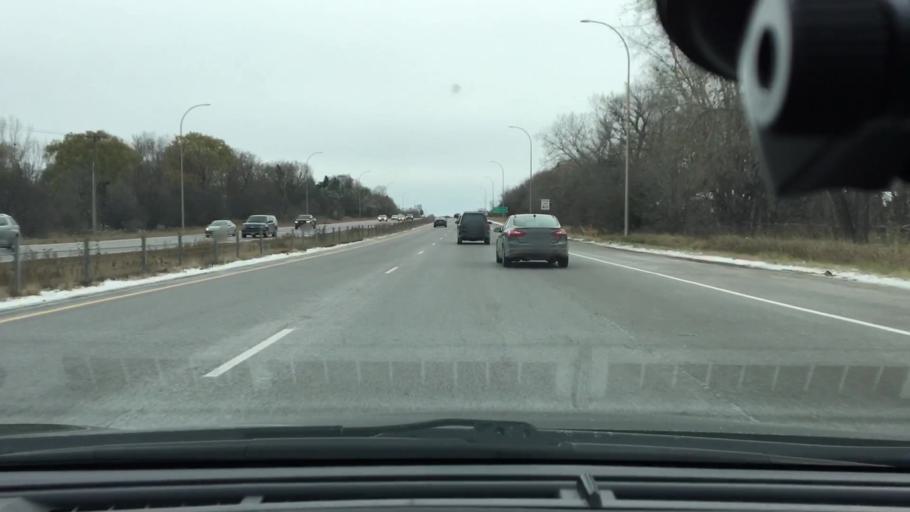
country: US
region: Minnesota
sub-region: Hennepin County
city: Osseo
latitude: 45.0783
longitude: -93.4020
